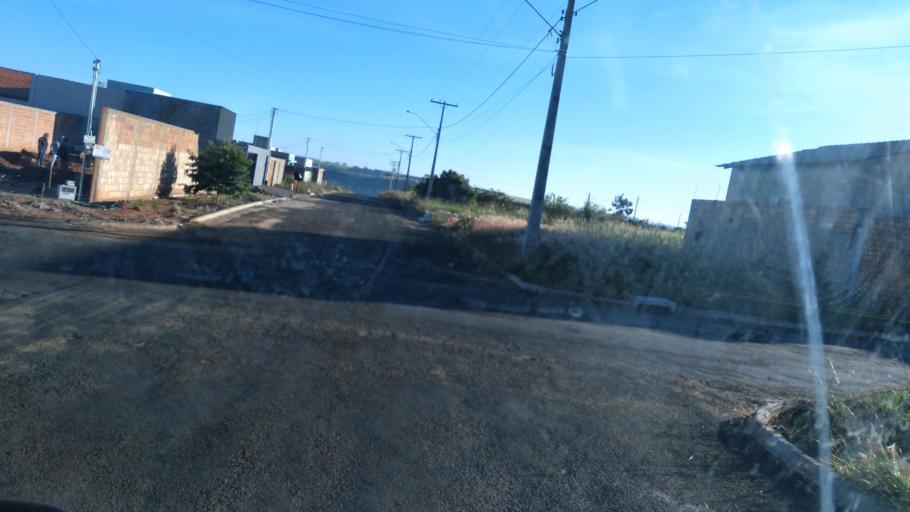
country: BR
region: Goias
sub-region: Mineiros
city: Mineiros
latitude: -17.5459
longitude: -52.5569
